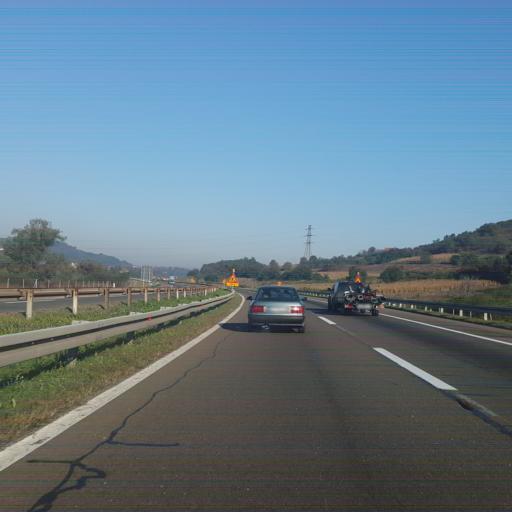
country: RS
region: Central Serbia
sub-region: Belgrade
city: Grocka
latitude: 44.6552
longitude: 20.6252
